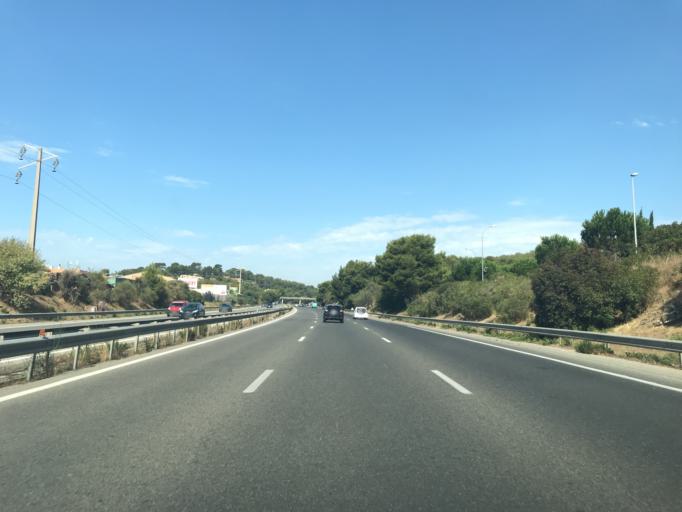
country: FR
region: Provence-Alpes-Cote d'Azur
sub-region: Departement du Var
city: Sanary-sur-Mer
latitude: 43.1267
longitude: 5.8238
